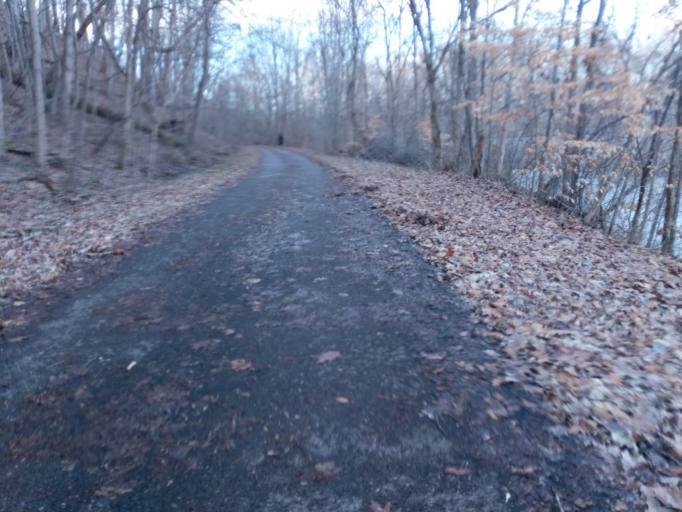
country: US
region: Ohio
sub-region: Athens County
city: Athens
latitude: 39.3546
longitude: -82.1074
